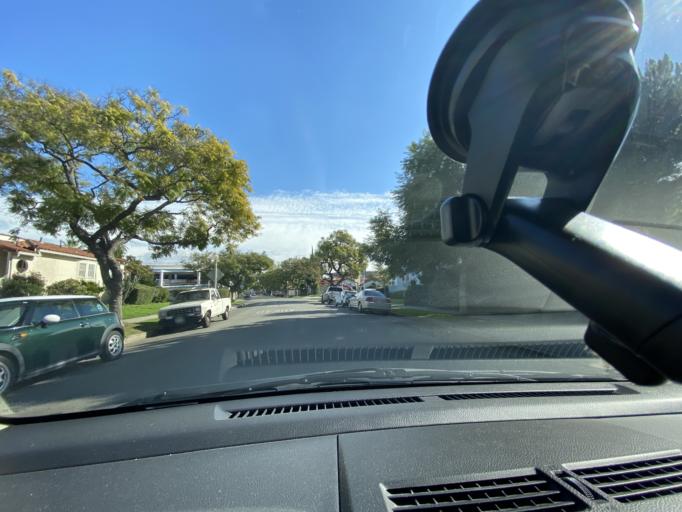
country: US
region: California
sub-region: Los Angeles County
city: Culver City
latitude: 34.0436
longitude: -118.3814
